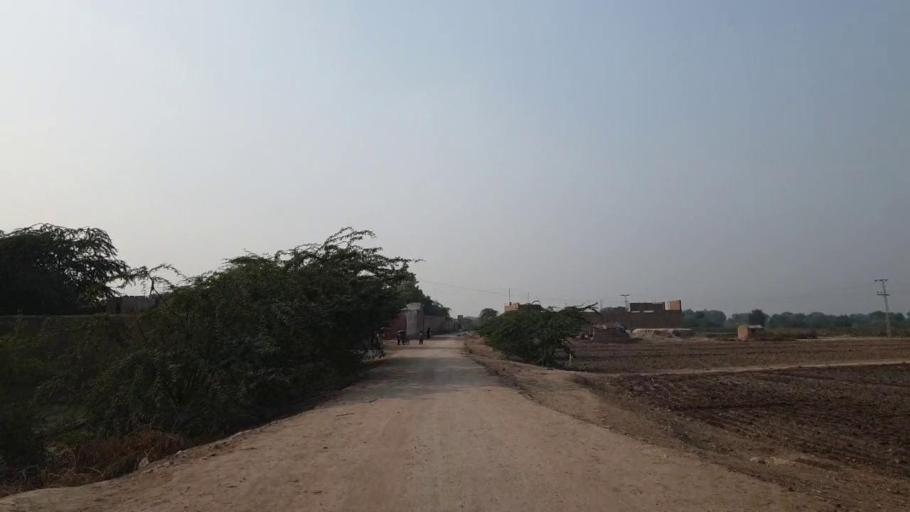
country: PK
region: Sindh
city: Bhan
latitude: 26.5578
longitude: 67.7128
